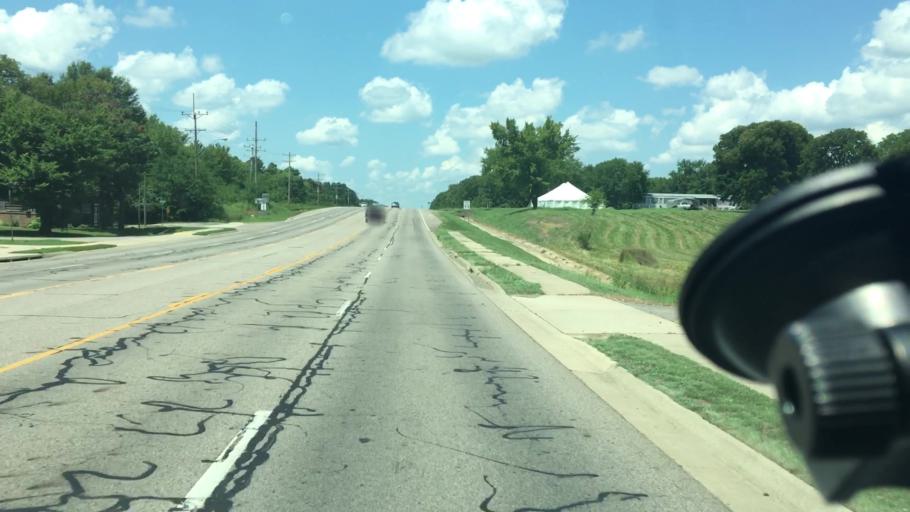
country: US
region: Arkansas
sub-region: Sebastian County
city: Barling
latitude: 35.3187
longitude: -94.2559
